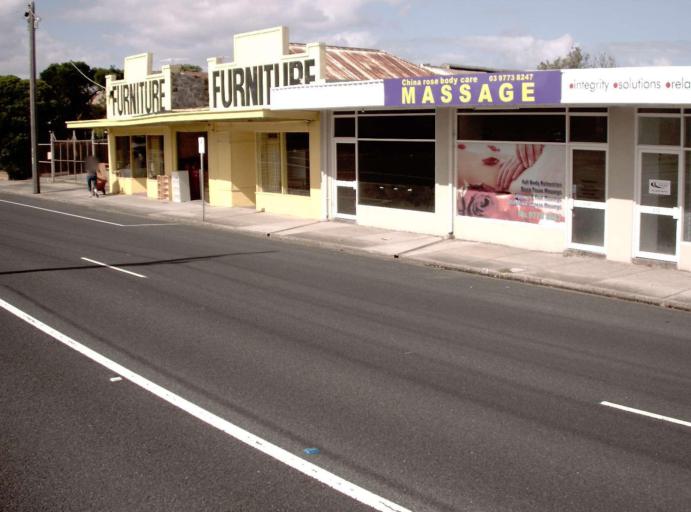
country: AU
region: Victoria
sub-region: Kingston
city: Bonbeach
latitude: -38.0611
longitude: 145.1193
